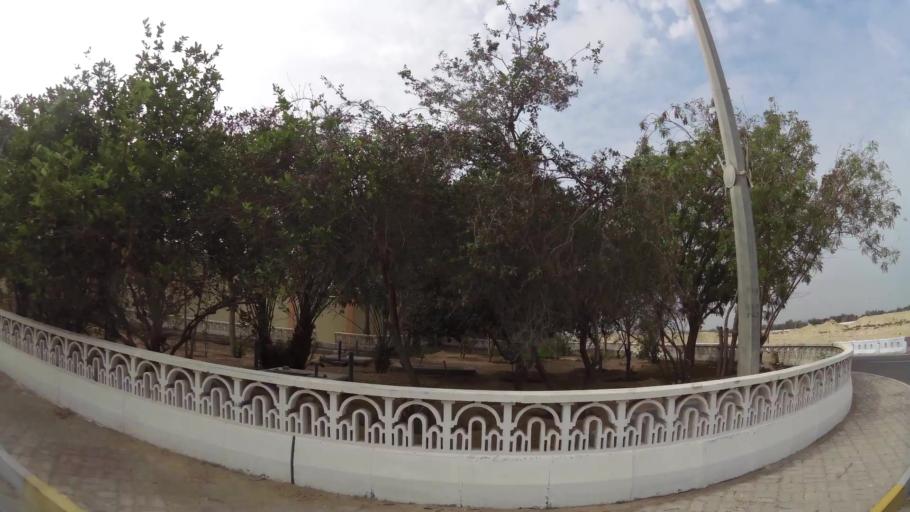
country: AE
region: Abu Dhabi
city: Abu Dhabi
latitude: 24.6492
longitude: 54.7294
